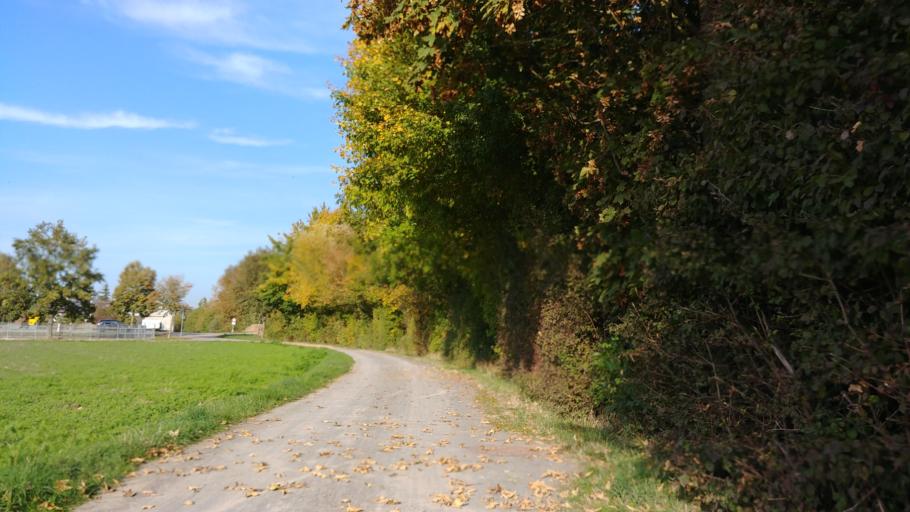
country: DE
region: Baden-Wuerttemberg
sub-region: Regierungsbezirk Stuttgart
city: Abstatt
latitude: 49.0560
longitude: 9.2739
